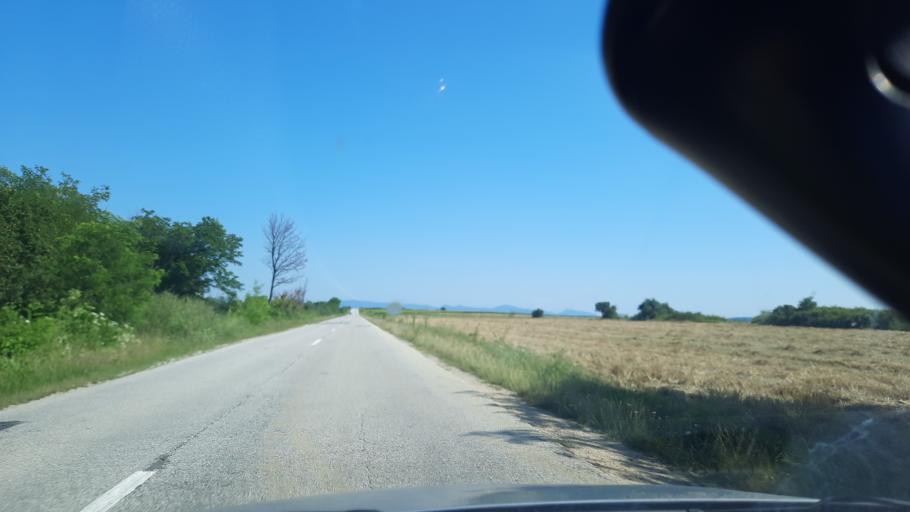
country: RS
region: Central Serbia
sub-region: Branicevski Okrug
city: Malo Crnice
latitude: 44.5702
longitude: 21.4274
